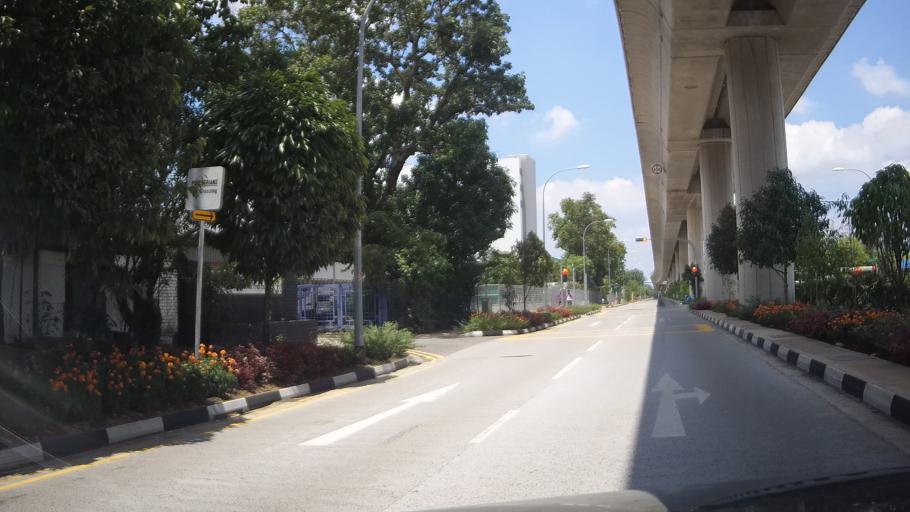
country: MY
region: Johor
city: Johor Bahru
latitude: 1.3276
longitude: 103.6758
